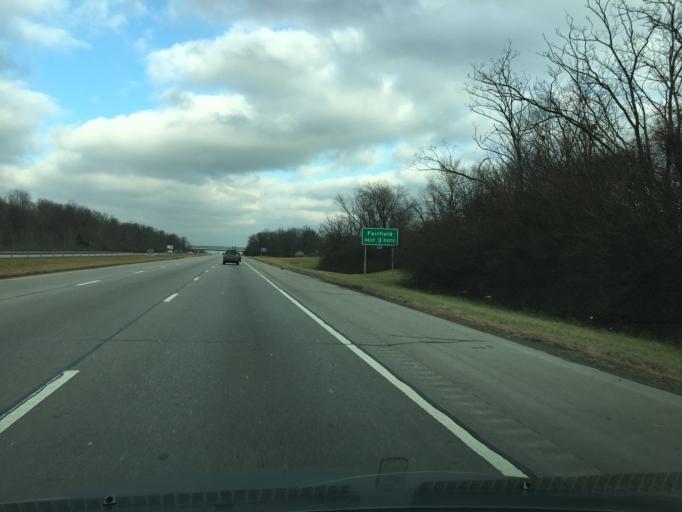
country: US
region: Ohio
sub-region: Hamilton County
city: Mount Healthy Heights
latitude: 39.2742
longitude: -84.5801
